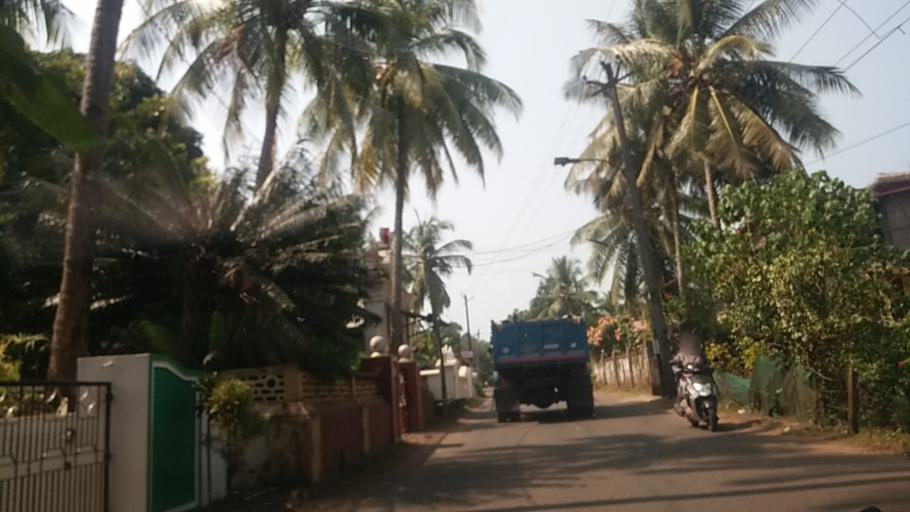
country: IN
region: Goa
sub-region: North Goa
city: Solim
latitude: 15.6162
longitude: 73.7887
